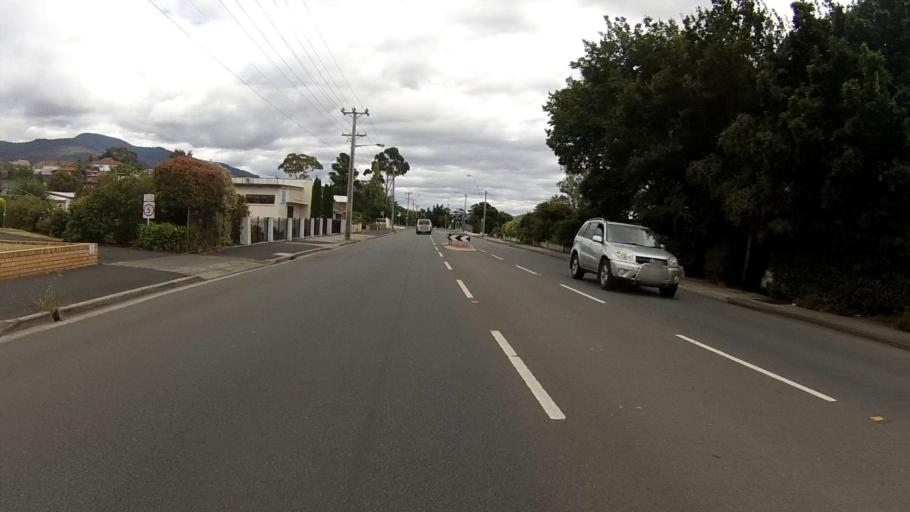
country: AU
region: Tasmania
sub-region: Glenorchy
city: Glenorchy
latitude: -42.8235
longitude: 147.2645
